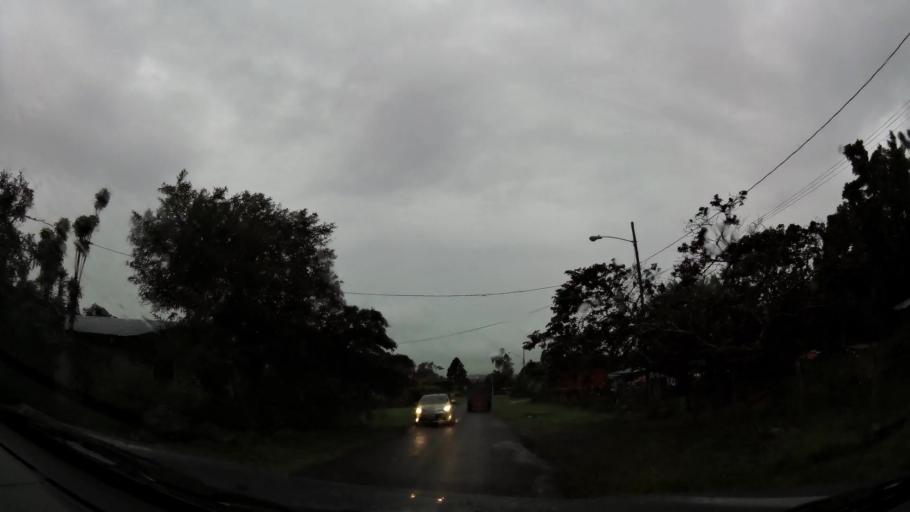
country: PA
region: Chiriqui
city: Volcan
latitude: 8.7906
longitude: -82.6476
